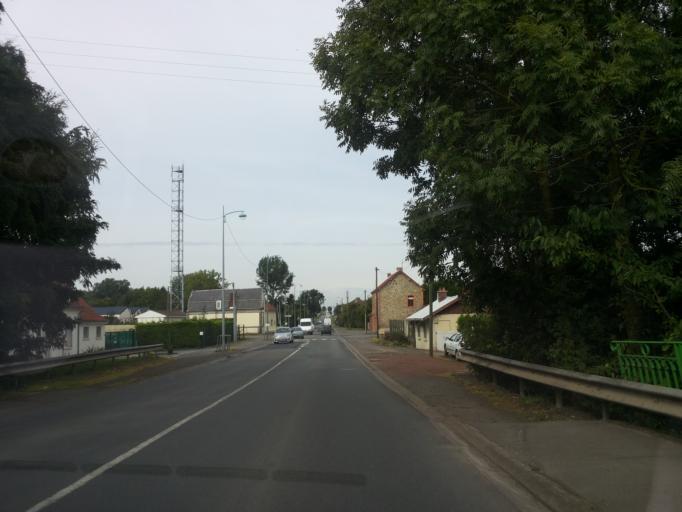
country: FR
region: Nord-Pas-de-Calais
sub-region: Departement du Pas-de-Calais
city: Marquion
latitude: 50.2132
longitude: 3.0782
